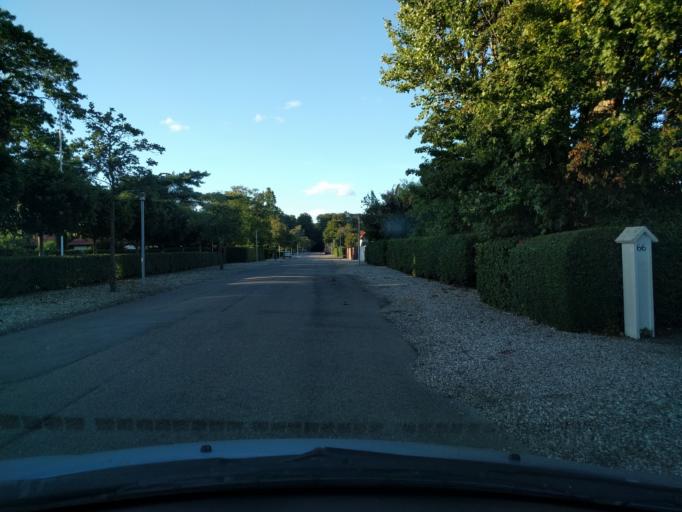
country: DK
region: South Denmark
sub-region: Nyborg Kommune
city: Nyborg
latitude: 55.3295
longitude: 10.8075
